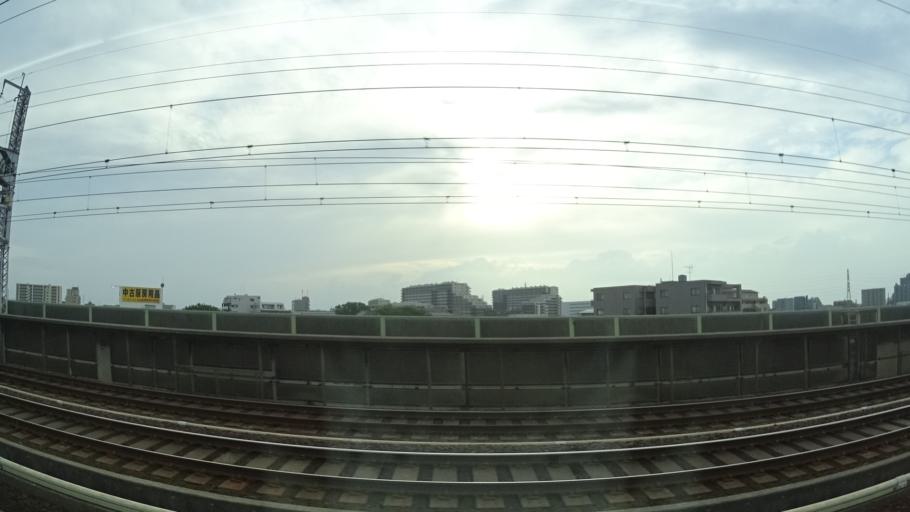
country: JP
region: Saitama
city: Ageoshimo
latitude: 35.9348
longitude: 139.6167
